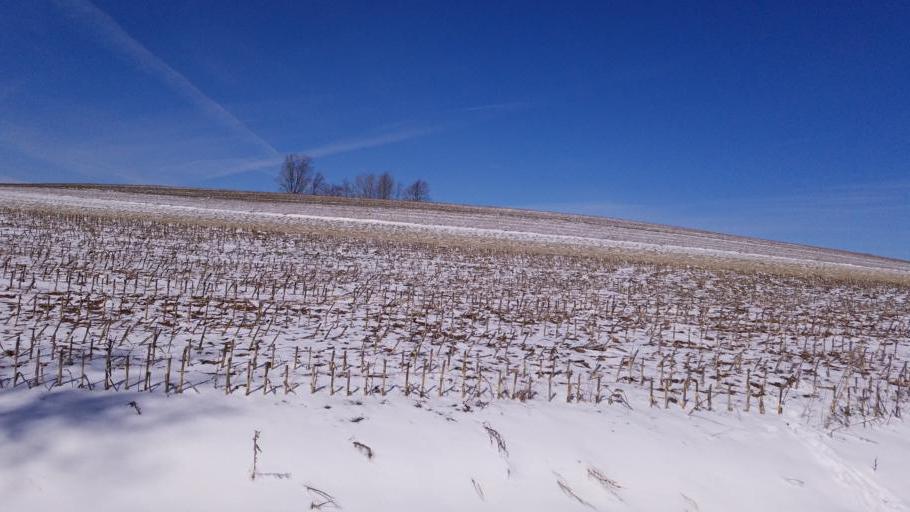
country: US
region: Pennsylvania
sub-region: Tioga County
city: Westfield
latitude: 41.9378
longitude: -77.7575
